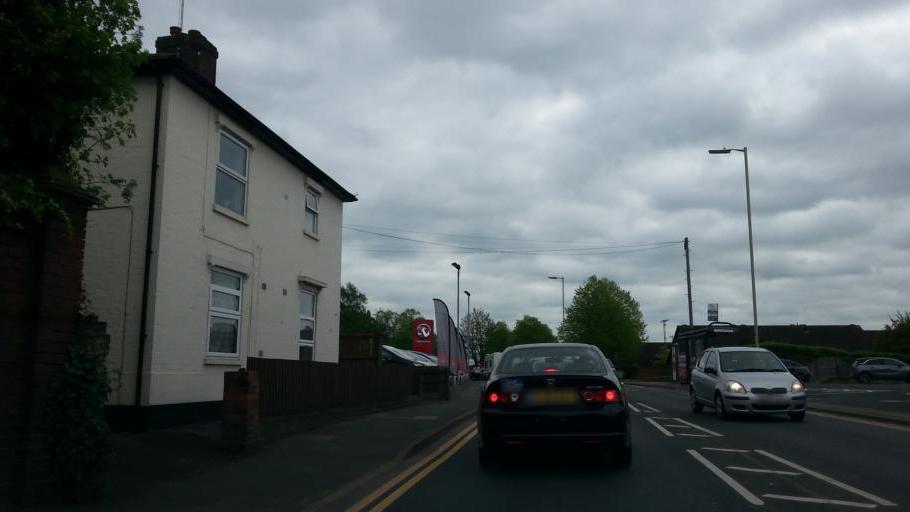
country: GB
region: England
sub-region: Dudley
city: Stourbridge
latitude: 52.4650
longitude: -2.1506
